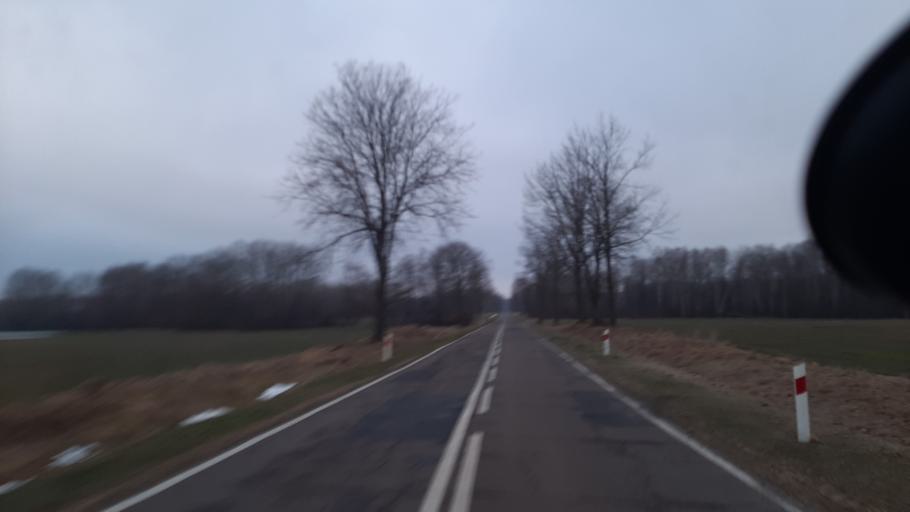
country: PL
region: Lublin Voivodeship
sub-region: Powiat parczewski
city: Sosnowica
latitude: 51.5976
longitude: 23.1482
